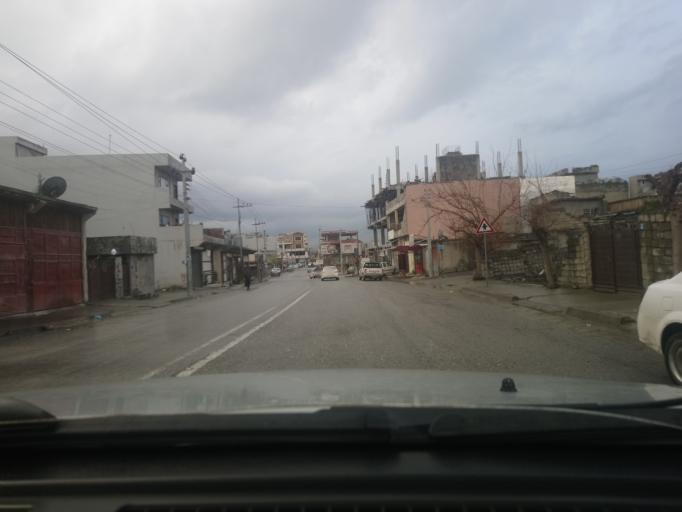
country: IQ
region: As Sulaymaniyah
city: Qeladize
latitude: 36.1845
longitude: 45.1298
